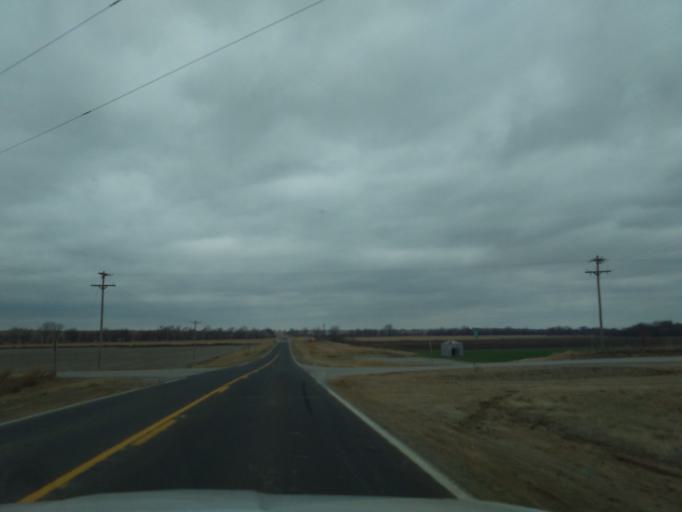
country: US
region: Nebraska
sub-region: Richardson County
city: Falls City
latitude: 40.0577
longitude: -95.5197
